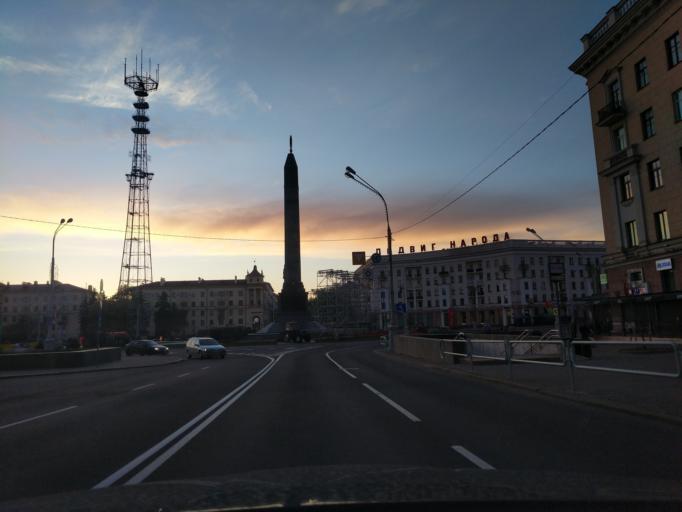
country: BY
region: Minsk
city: Minsk
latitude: 53.9080
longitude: 27.5761
